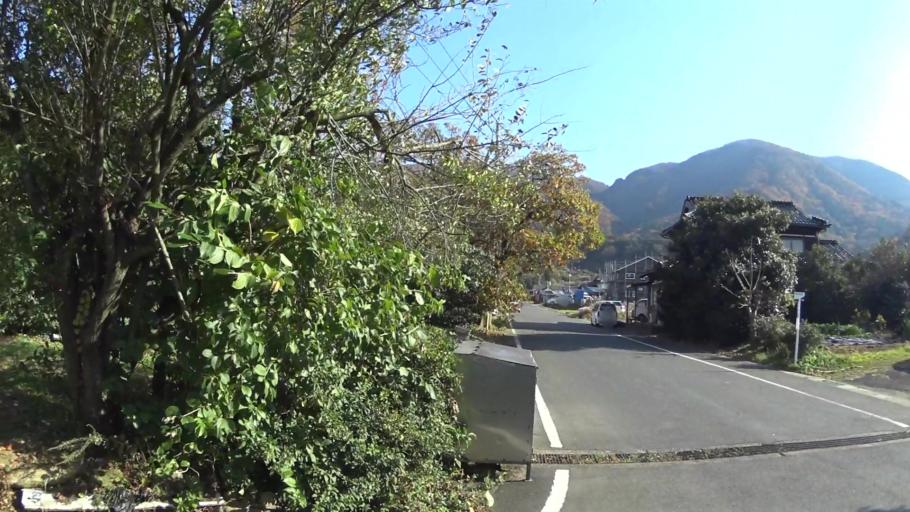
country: JP
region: Kyoto
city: Maizuru
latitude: 35.5600
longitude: 135.4006
